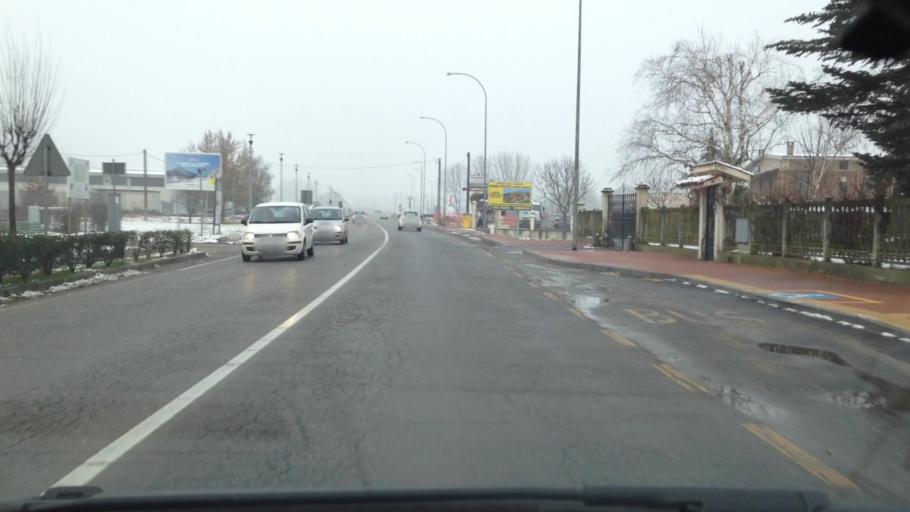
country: IT
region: Piedmont
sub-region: Provincia di Asti
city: Montegrosso
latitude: 44.8199
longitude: 8.2328
